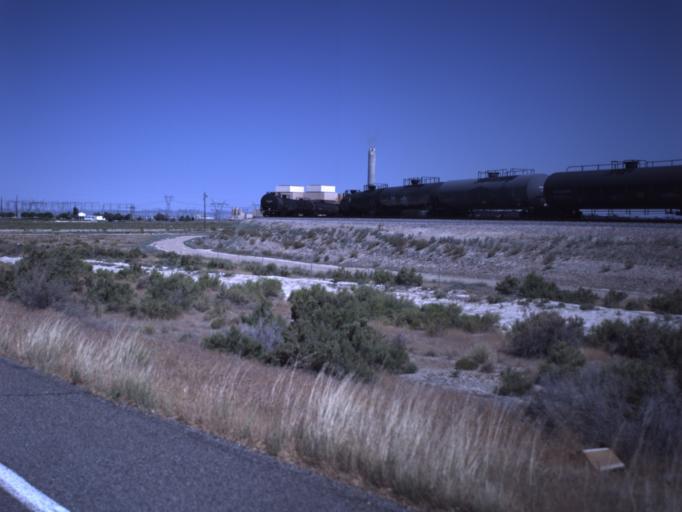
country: US
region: Utah
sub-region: Millard County
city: Delta
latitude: 39.4913
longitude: -112.5618
